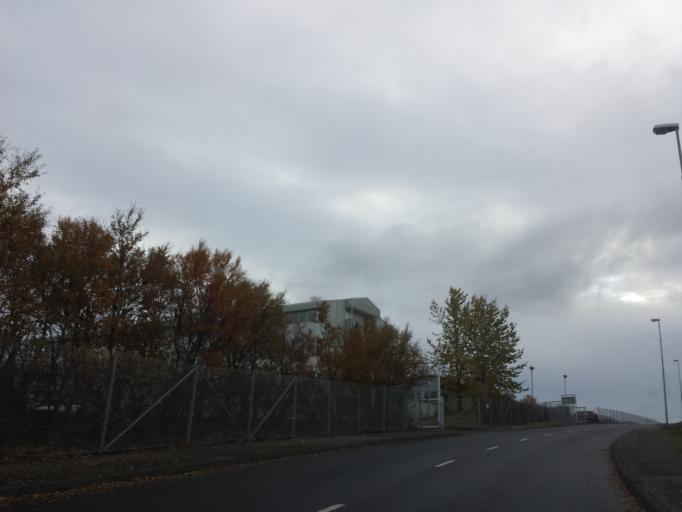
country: IS
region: Capital Region
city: Mosfellsbaer
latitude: 64.1205
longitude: -21.7927
